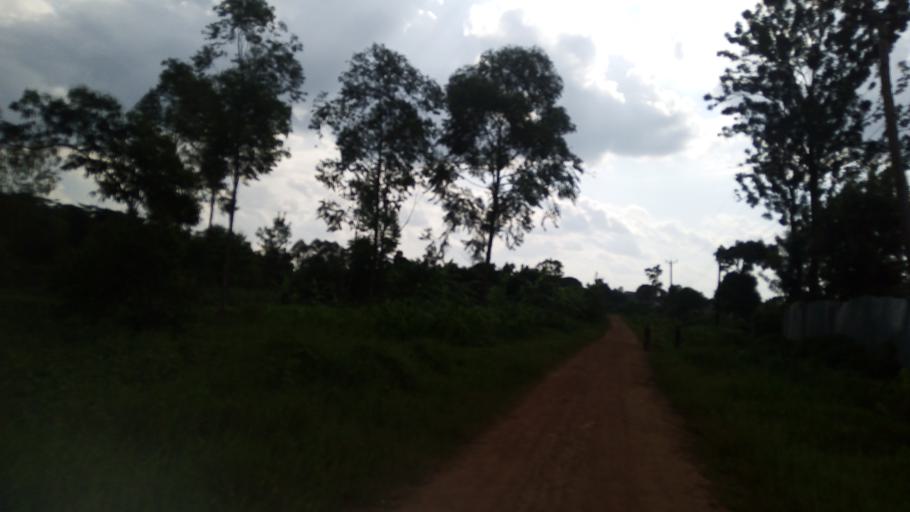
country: UG
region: Eastern Region
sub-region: Mbale District
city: Mbale
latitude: 1.0757
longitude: 34.1558
